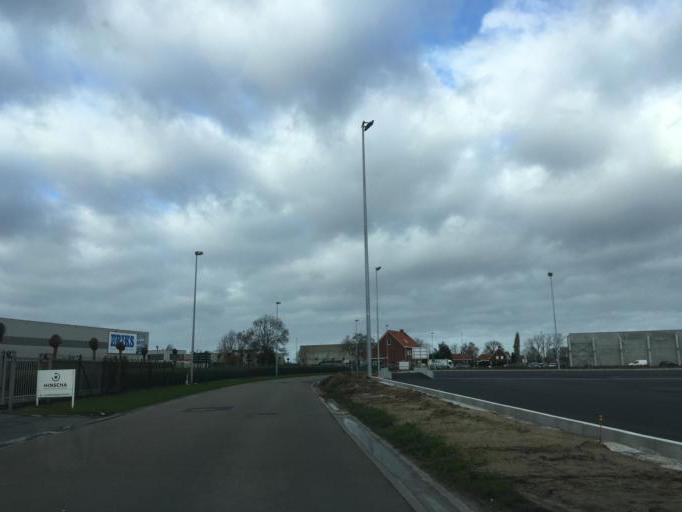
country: BE
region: Flanders
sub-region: Provincie West-Vlaanderen
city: Roeselare
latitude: 50.9790
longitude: 3.1328
